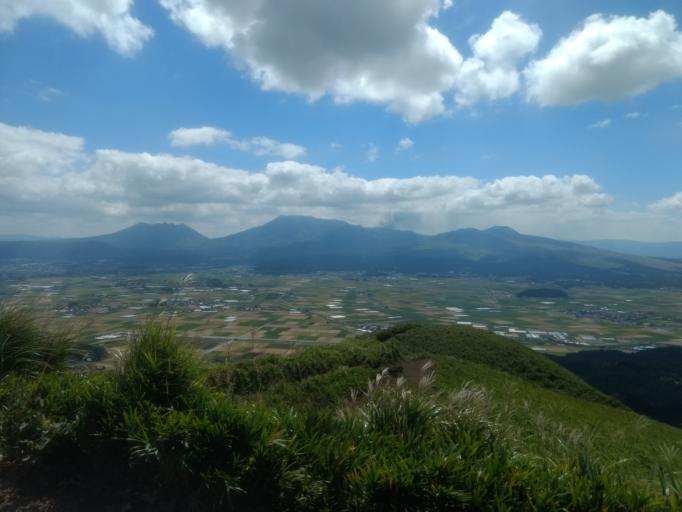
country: JP
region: Kumamoto
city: Aso
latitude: 32.9956
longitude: 131.0670
